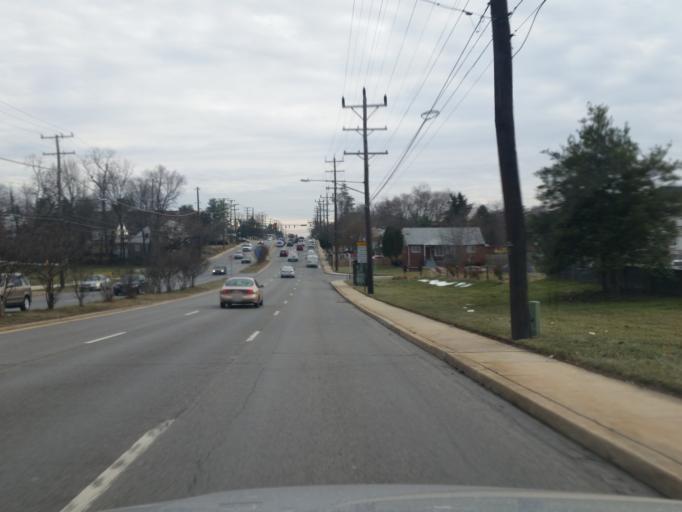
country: US
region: Maryland
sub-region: Montgomery County
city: Wheaton
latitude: 39.0276
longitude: -77.0470
